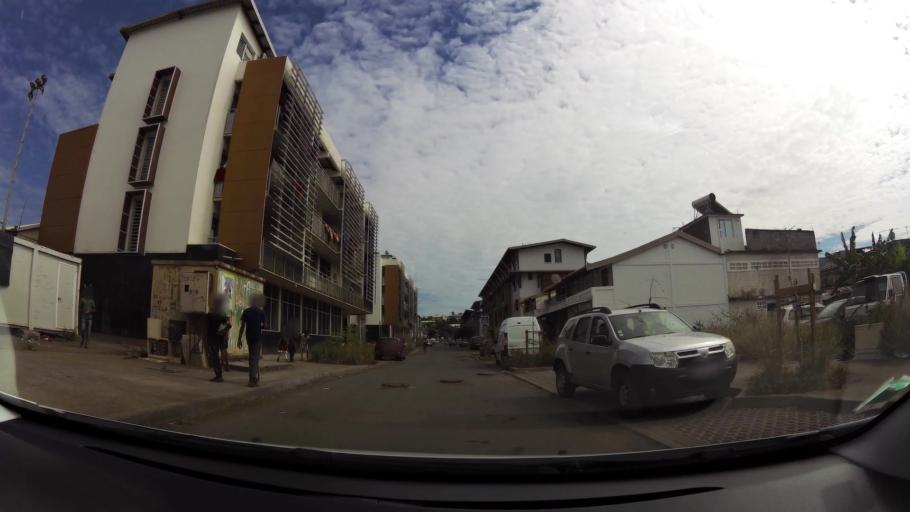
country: YT
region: Mamoudzou
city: Mamoudzou
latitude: -12.7827
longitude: 45.2334
